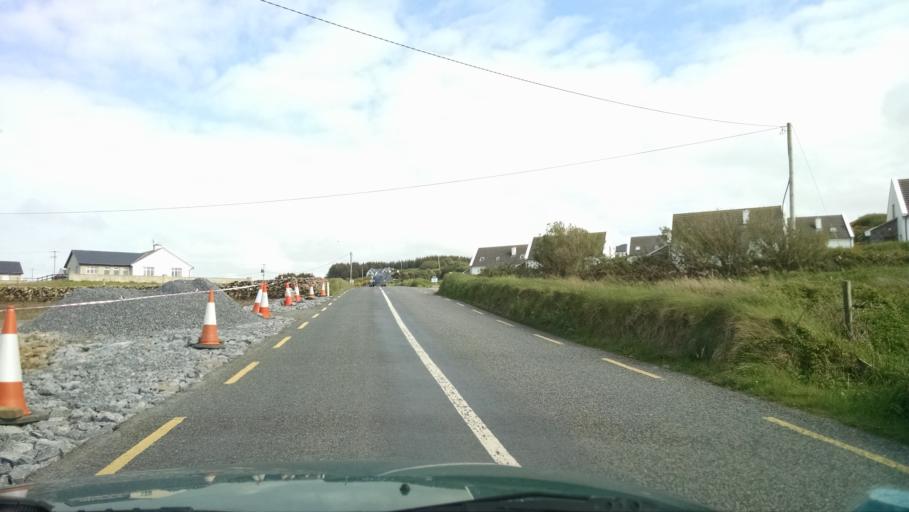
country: IE
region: Connaught
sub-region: County Galway
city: Bearna
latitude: 53.0090
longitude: -9.3579
